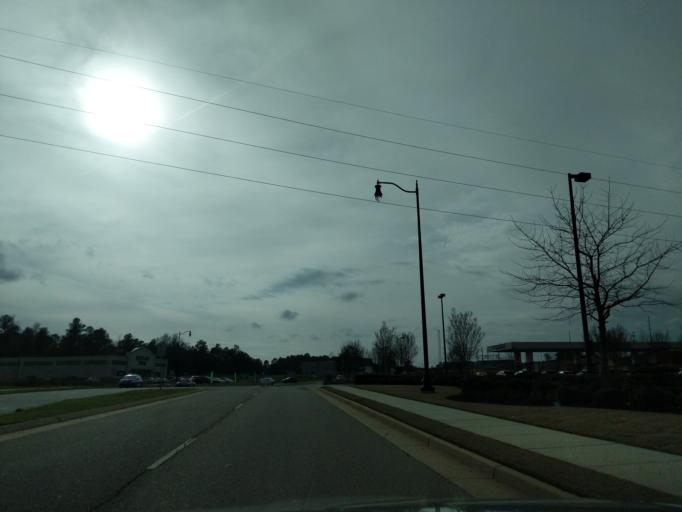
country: US
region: Georgia
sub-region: Columbia County
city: Martinez
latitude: 33.5239
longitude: -82.0198
